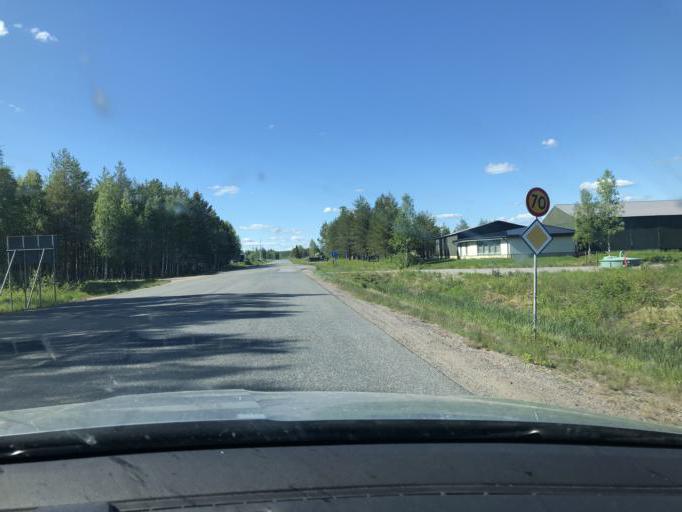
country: SE
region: Norrbotten
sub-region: Kalix Kommun
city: Kalix
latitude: 65.8468
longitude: 23.1992
